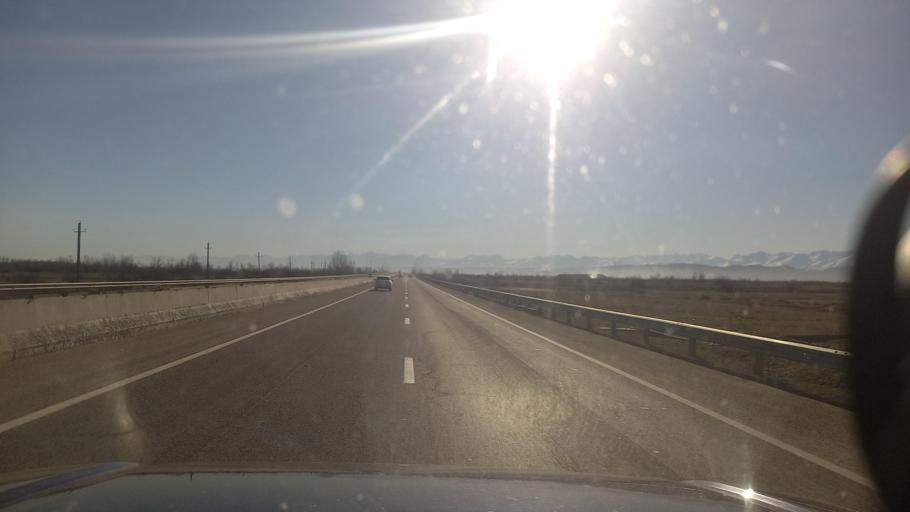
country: RU
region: Kabardino-Balkariya
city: Kishpek
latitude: 43.6058
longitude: 43.6589
